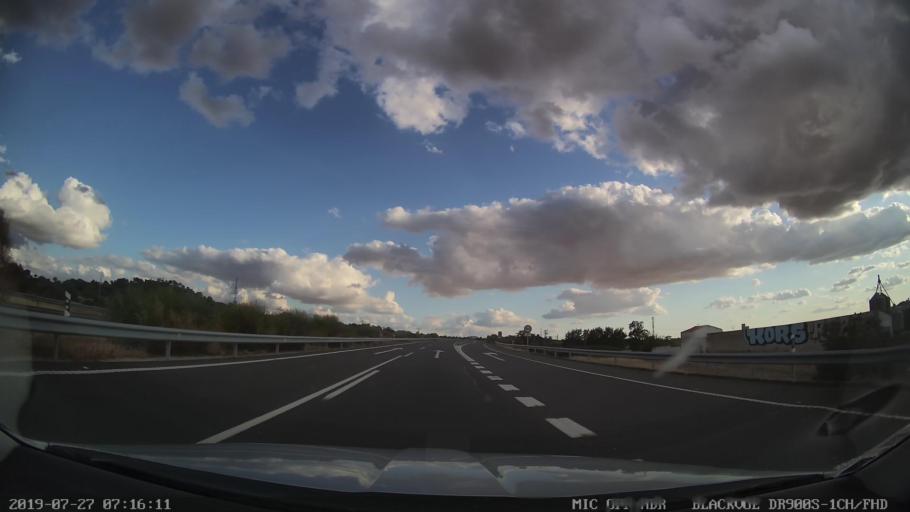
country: ES
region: Extremadura
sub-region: Provincia de Caceres
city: Trujillo
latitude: 39.4605
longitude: -5.8605
